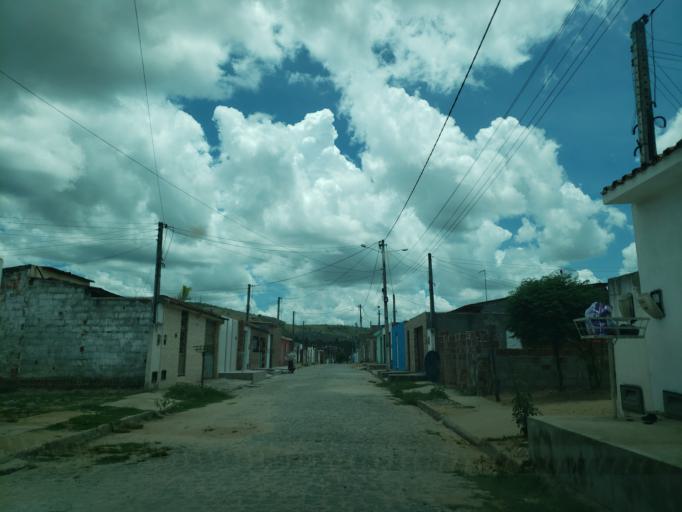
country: BR
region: Alagoas
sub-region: Uniao Dos Palmares
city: Uniao dos Palmares
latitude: -9.1491
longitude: -36.0091
